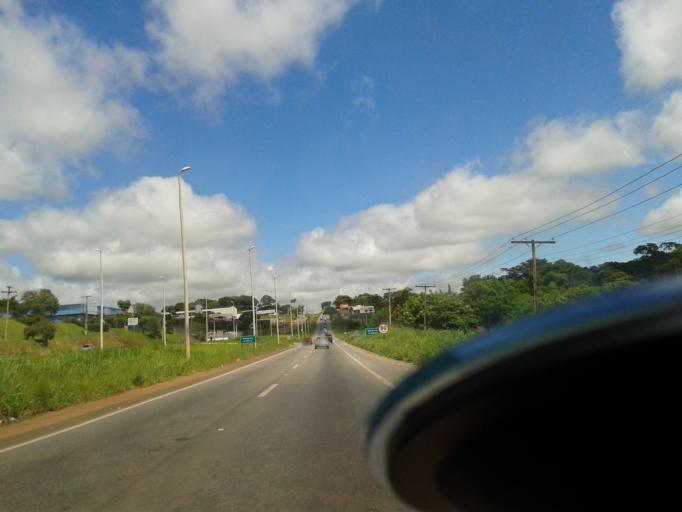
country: BR
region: Goias
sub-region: Goiania
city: Goiania
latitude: -16.6360
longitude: -49.3451
